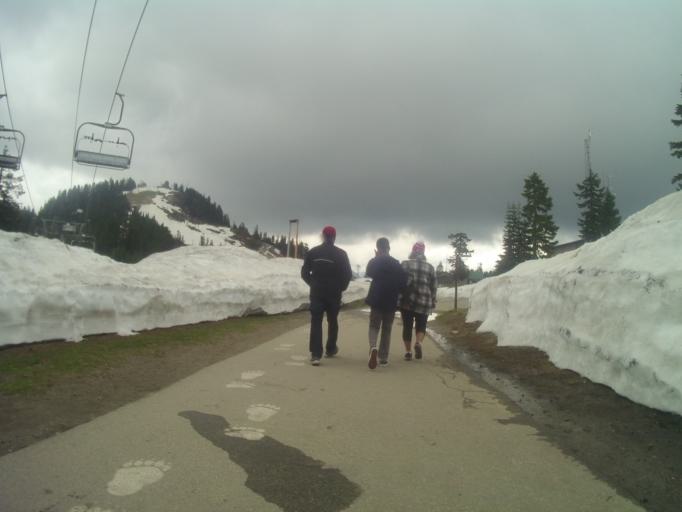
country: CA
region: British Columbia
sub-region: Fraser Valley Regional District
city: North Vancouver
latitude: 49.3807
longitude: -123.0808
